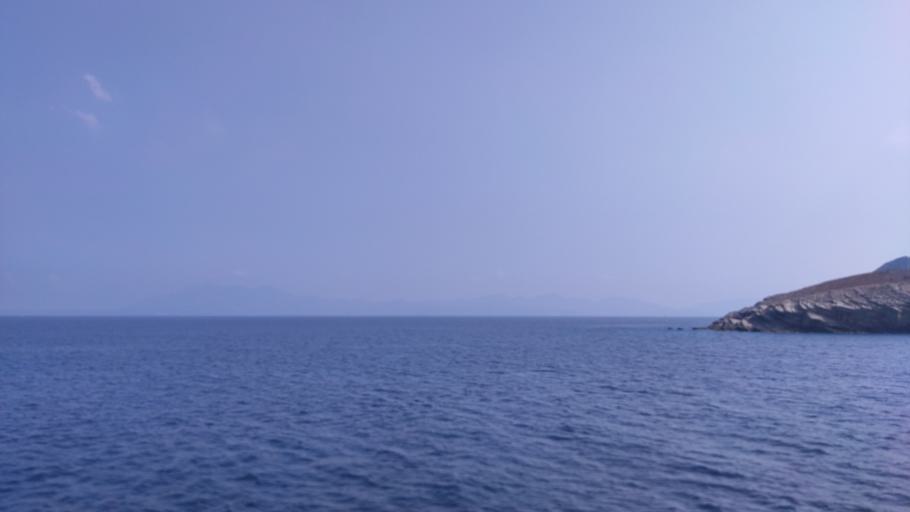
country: GR
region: South Aegean
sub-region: Nomos Dodekanisou
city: Symi
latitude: 36.6442
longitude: 27.8070
